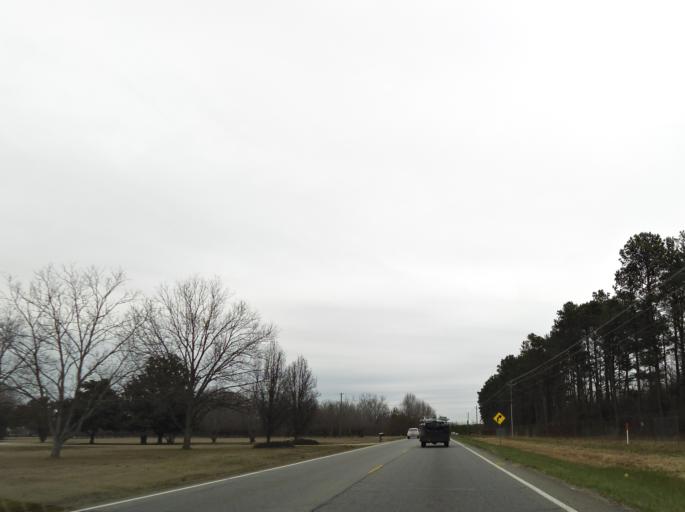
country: US
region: Georgia
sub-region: Peach County
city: Byron
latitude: 32.6698
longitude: -83.7296
